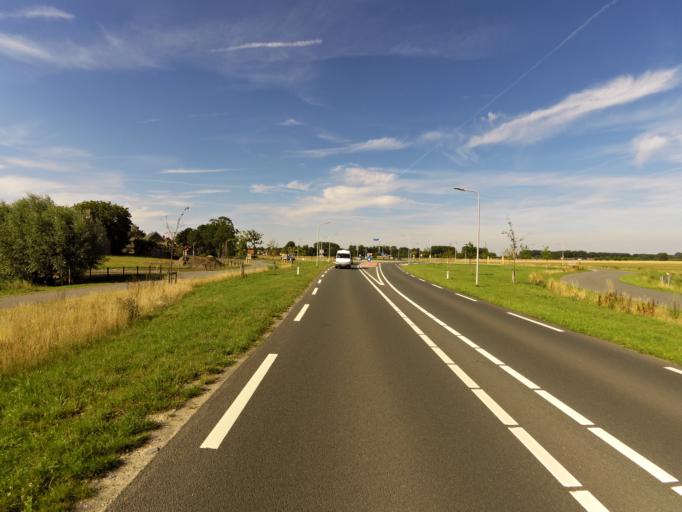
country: BE
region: Flanders
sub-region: Provincie Oost-Vlaanderen
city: Maldegem
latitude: 51.2649
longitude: 3.4541
